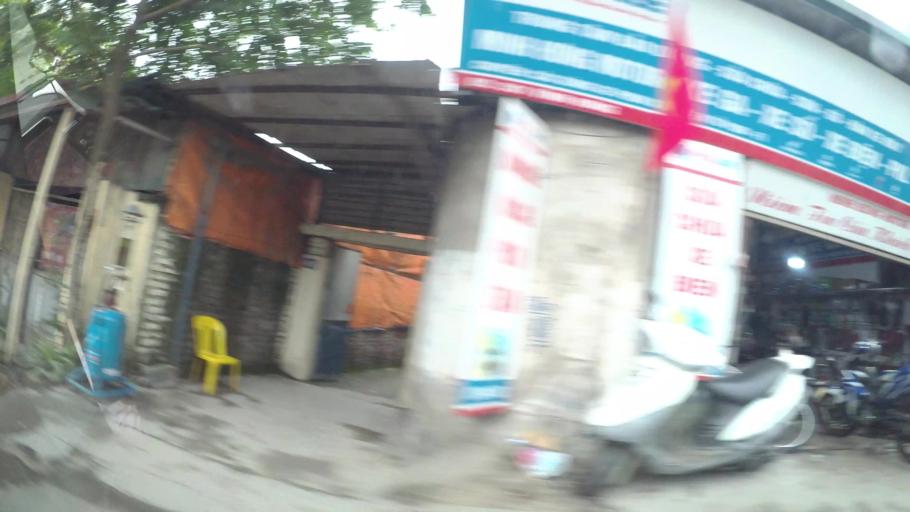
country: VN
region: Ha Noi
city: Hai BaTrung
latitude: 21.0005
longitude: 105.8794
